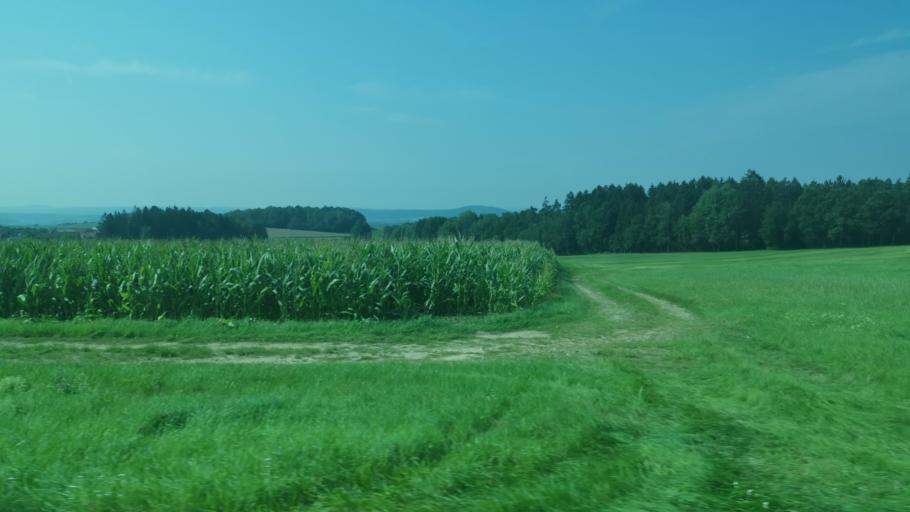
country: DE
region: Bavaria
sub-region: Upper Palatinate
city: Pemfling
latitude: 49.2599
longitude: 12.6364
